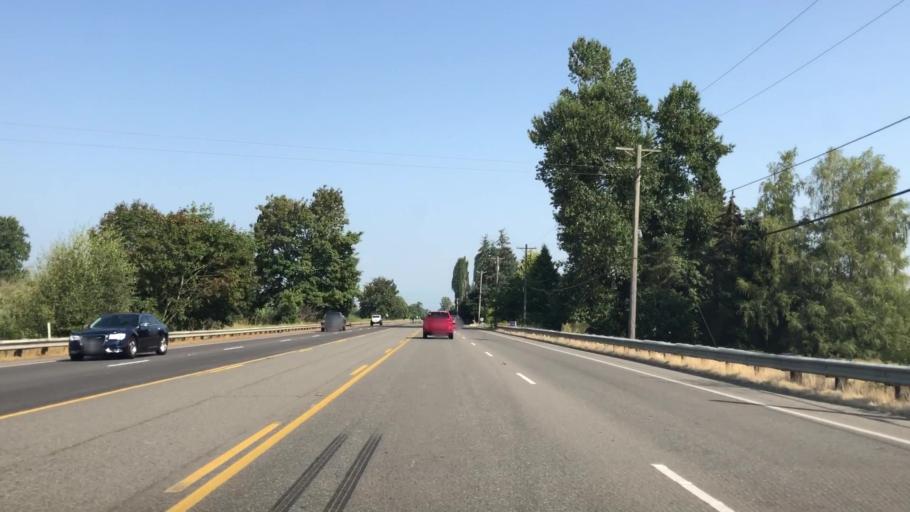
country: US
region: Washington
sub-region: Pierce County
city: Fife
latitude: 47.2309
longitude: -122.3802
